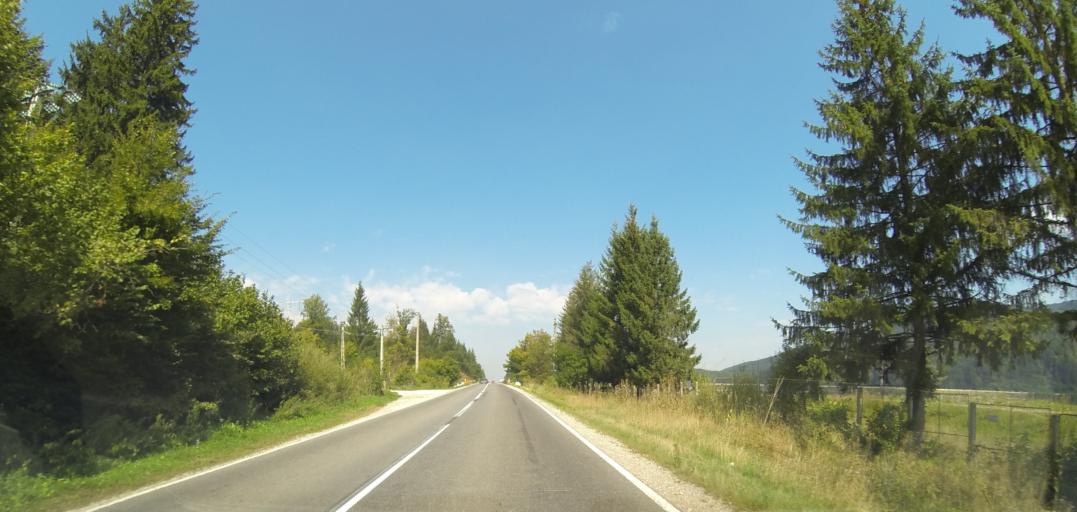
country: RO
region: Brasov
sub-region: Comuna Tarlungeni
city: Tarlungeni
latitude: 45.5776
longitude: 25.7621
